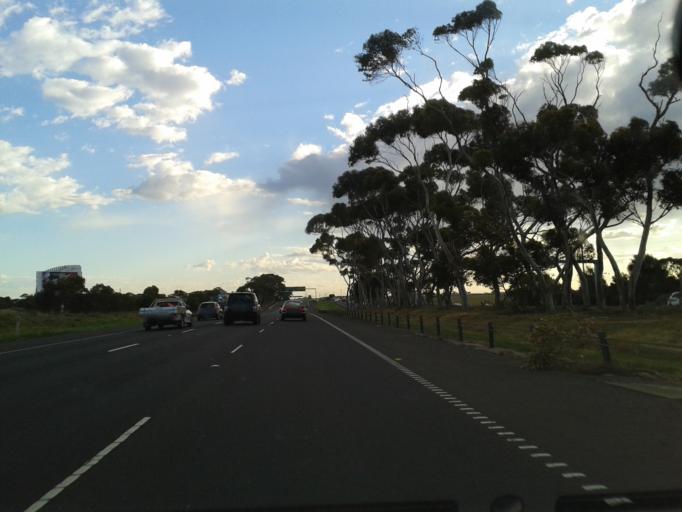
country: AU
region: Victoria
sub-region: Greater Geelong
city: Lara
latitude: -38.0431
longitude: 144.4083
